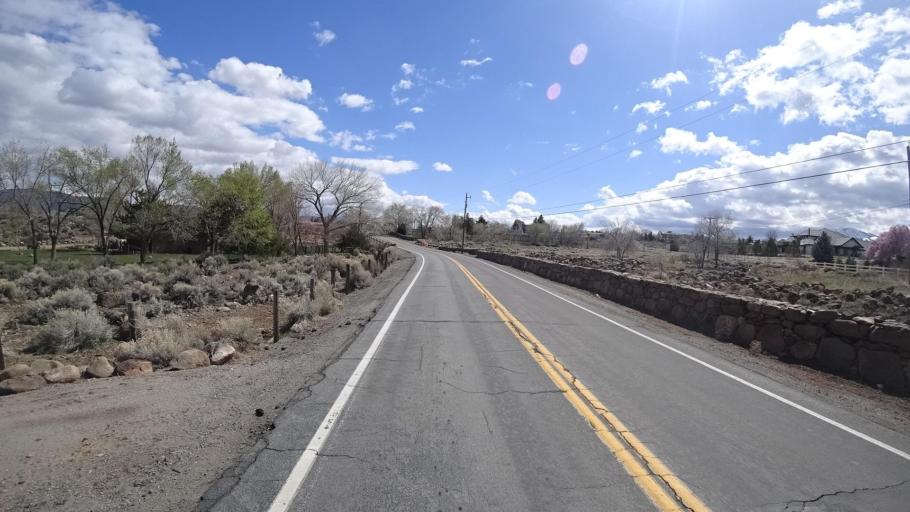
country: US
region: Nevada
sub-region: Washoe County
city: Reno
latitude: 39.4292
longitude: -119.7866
